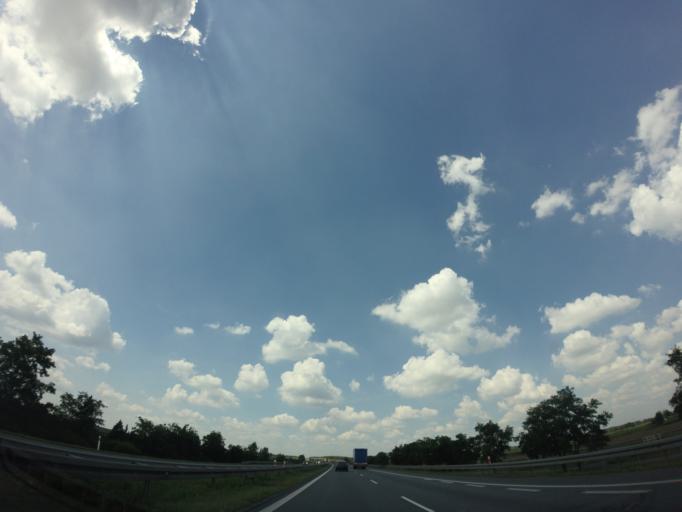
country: PL
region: Opole Voivodeship
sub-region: Powiat opolski
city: Proszkow
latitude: 50.5728
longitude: 17.8540
